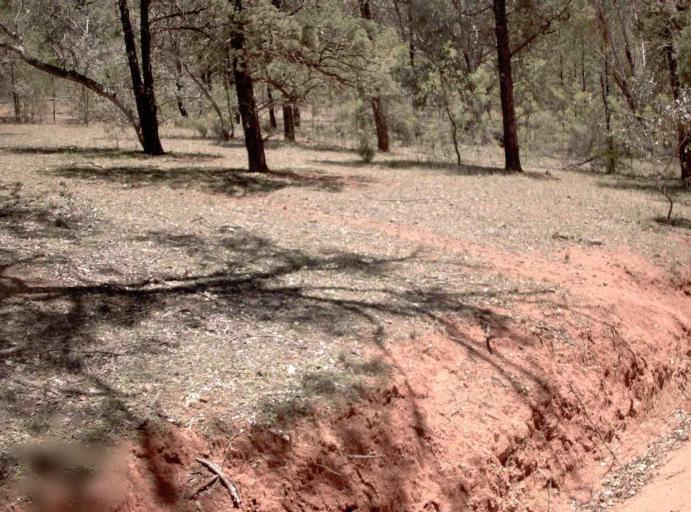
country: AU
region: New South Wales
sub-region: Snowy River
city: Jindabyne
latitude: -36.8902
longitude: 148.4213
